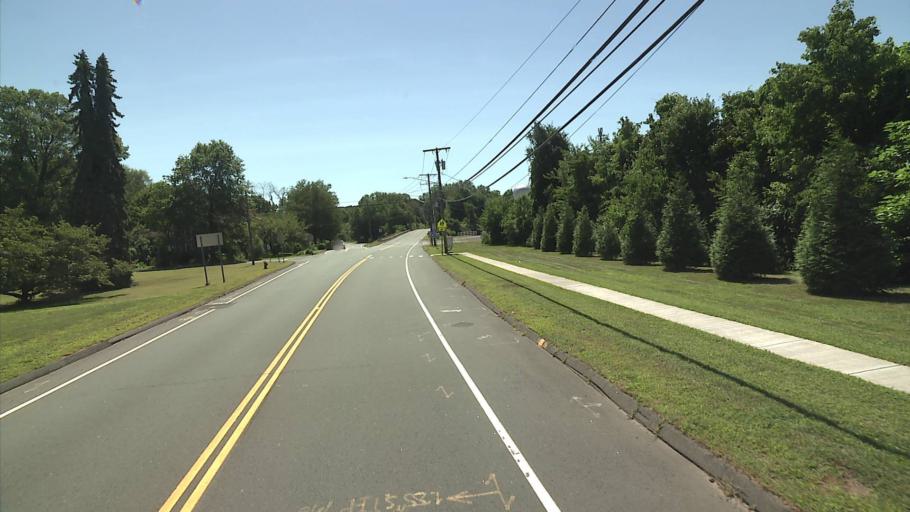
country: US
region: Connecticut
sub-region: New Haven County
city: Cheshire Village
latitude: 41.5663
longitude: -72.8925
